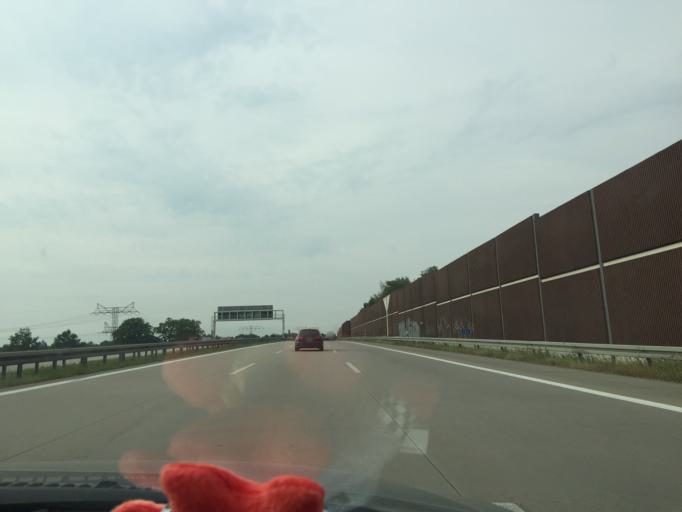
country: DE
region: Brandenburg
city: Petershagen
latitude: 52.5063
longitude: 13.7391
